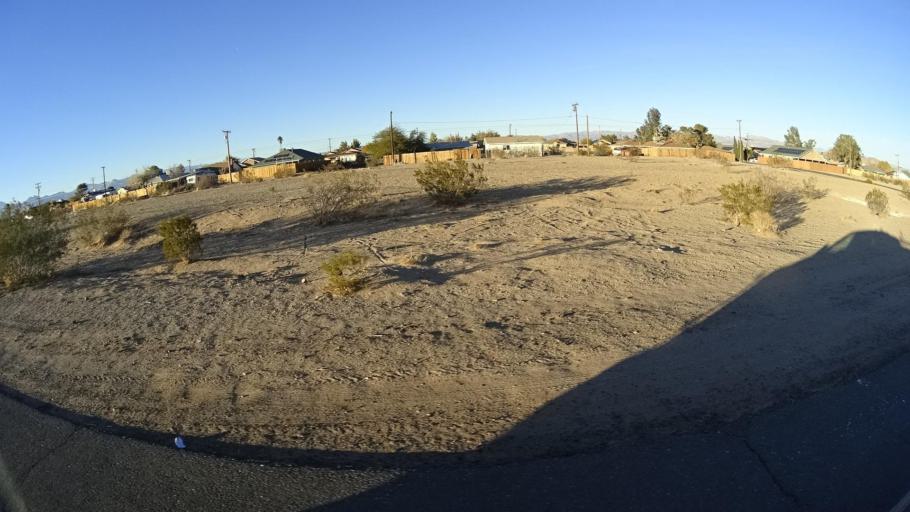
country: US
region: California
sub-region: Kern County
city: Ridgecrest
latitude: 35.6079
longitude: -117.6975
